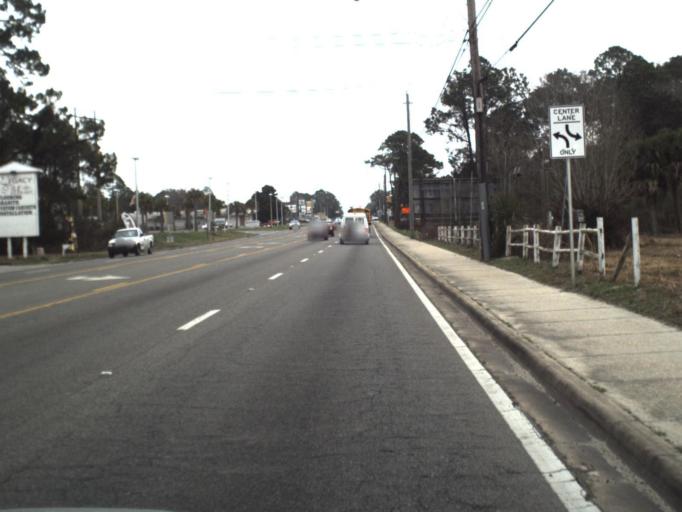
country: US
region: Florida
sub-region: Bay County
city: Cedar Grove
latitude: 30.1748
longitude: -85.6289
